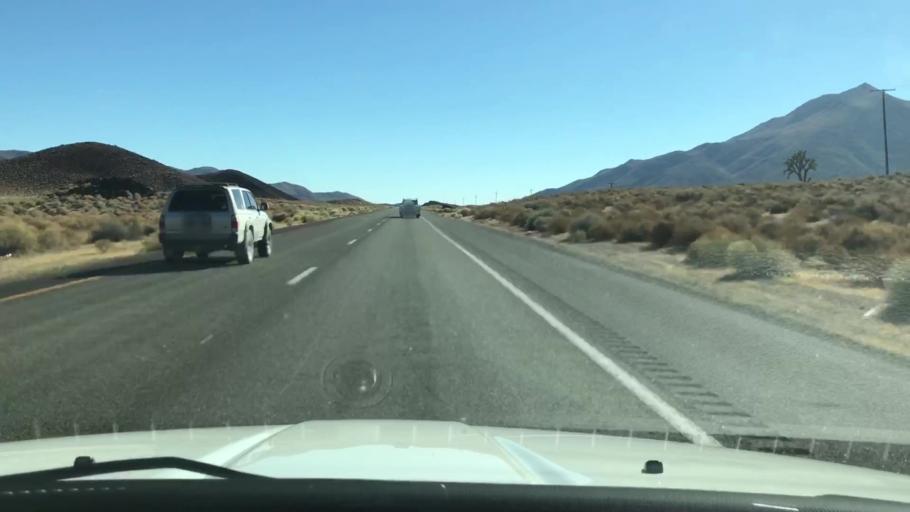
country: US
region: California
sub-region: Kern County
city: Inyokern
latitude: 35.9909
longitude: -117.9298
